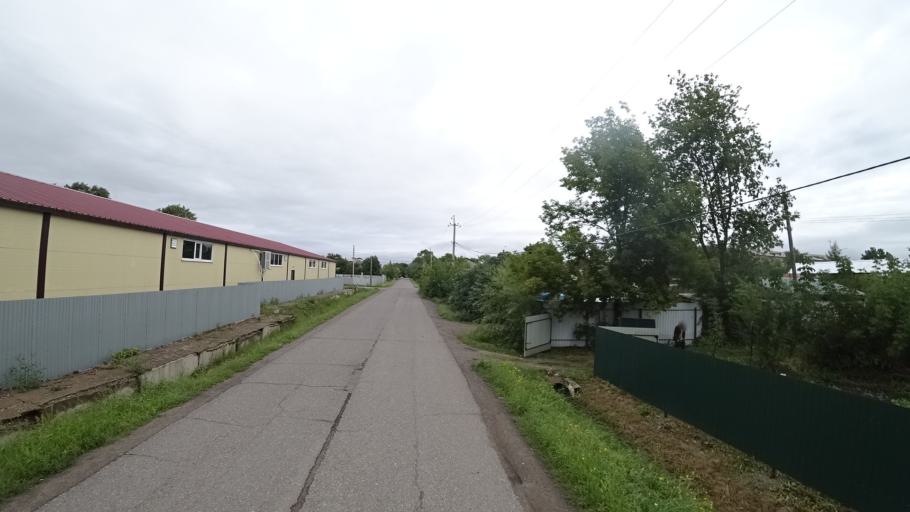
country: RU
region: Primorskiy
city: Chernigovka
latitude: 44.3397
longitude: 132.5756
